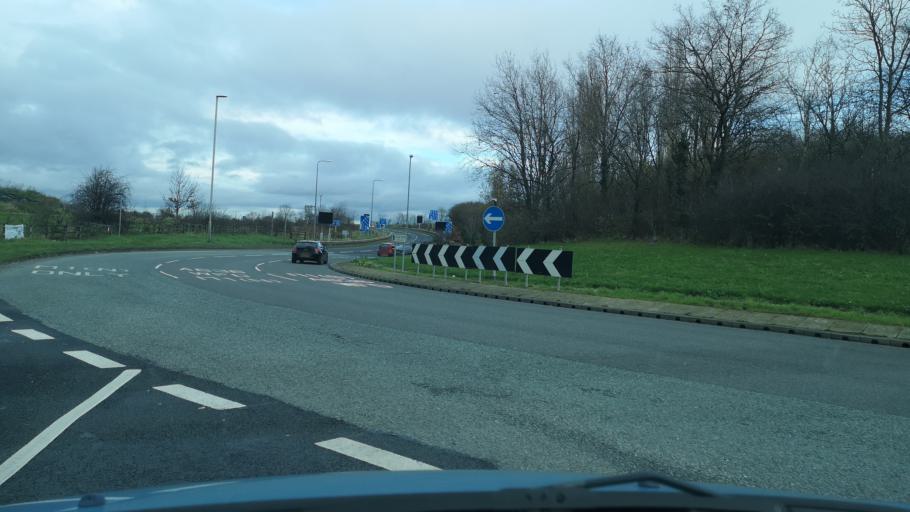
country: GB
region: England
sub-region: City and Borough of Wakefield
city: Crigglestone
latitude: 53.6504
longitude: -1.5309
